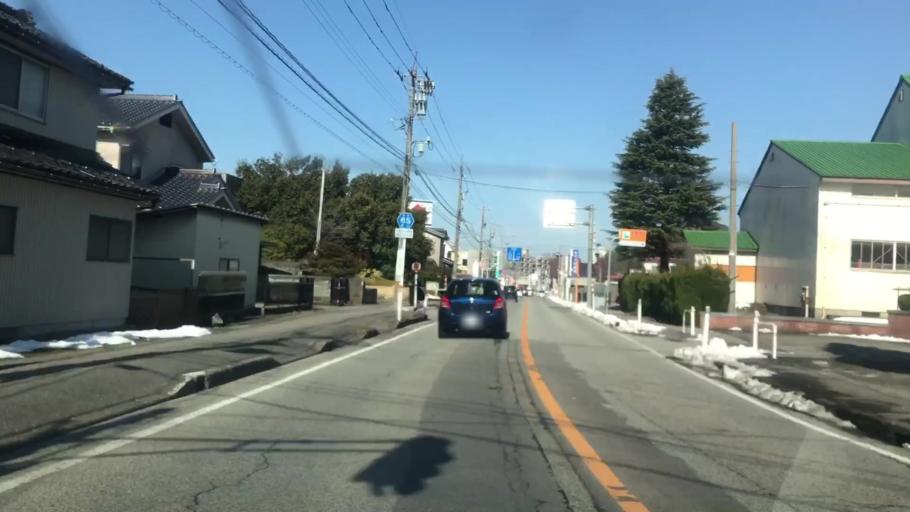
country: JP
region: Toyama
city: Toyama-shi
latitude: 36.6680
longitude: 137.2390
